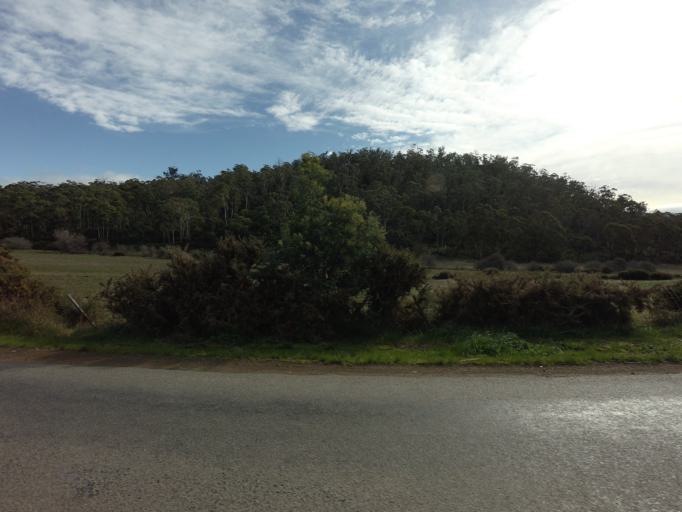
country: AU
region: Tasmania
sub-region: Derwent Valley
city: New Norfolk
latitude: -42.7810
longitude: 147.0086
